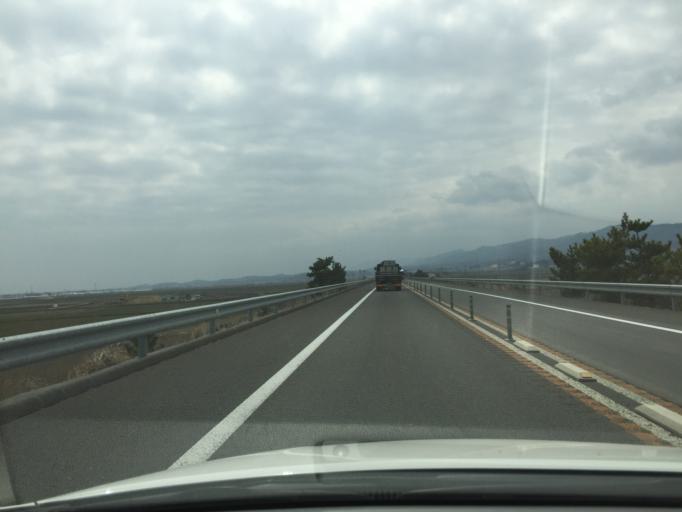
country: JP
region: Miyagi
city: Watari
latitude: 37.9995
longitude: 140.8799
